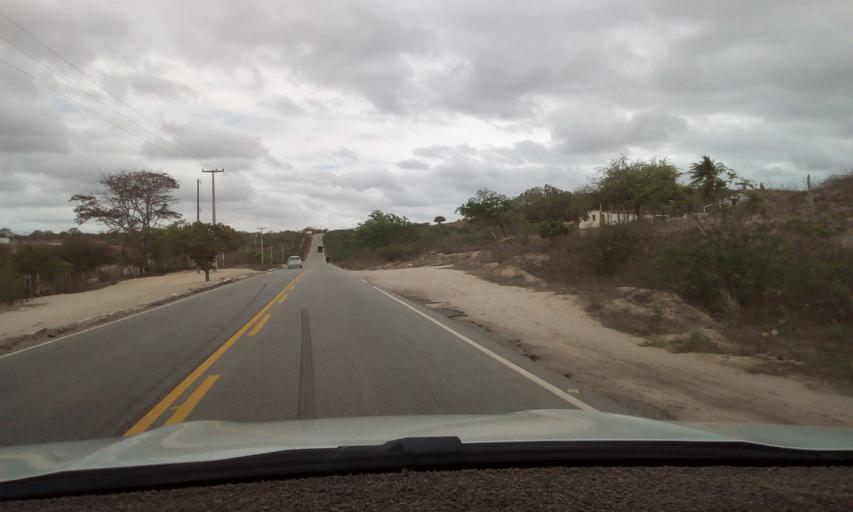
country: BR
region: Paraiba
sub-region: Picui
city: Picui
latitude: -6.5922
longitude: -36.2383
